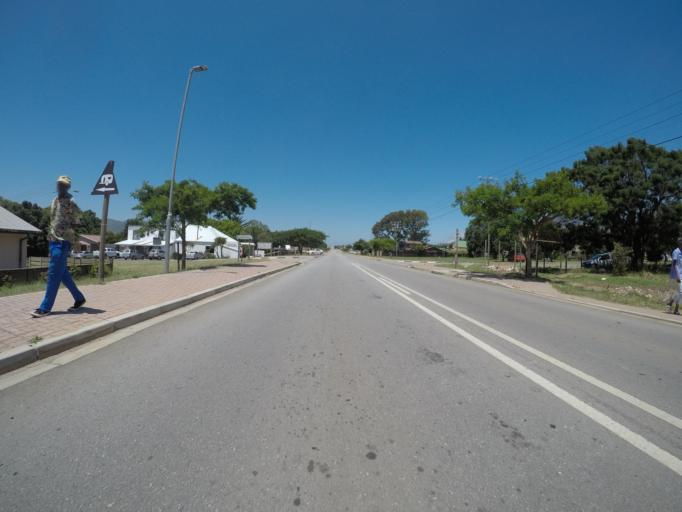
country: ZA
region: Eastern Cape
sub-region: Cacadu District Municipality
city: Kareedouw
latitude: -33.9516
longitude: 24.2893
